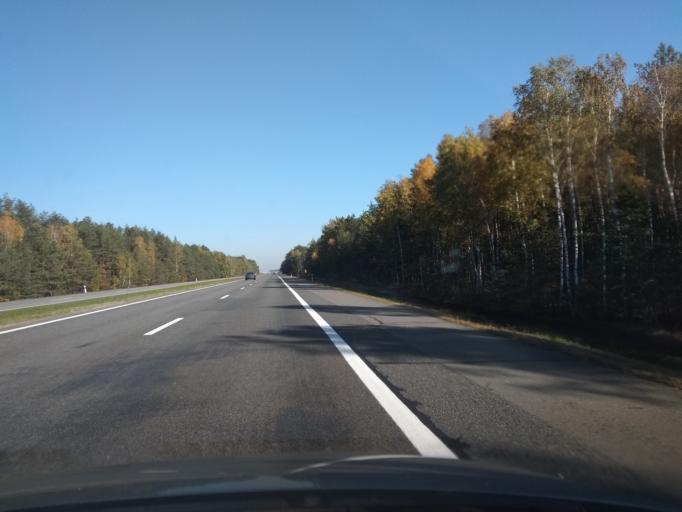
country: BY
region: Brest
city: Antopal'
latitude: 52.3770
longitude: 24.7539
